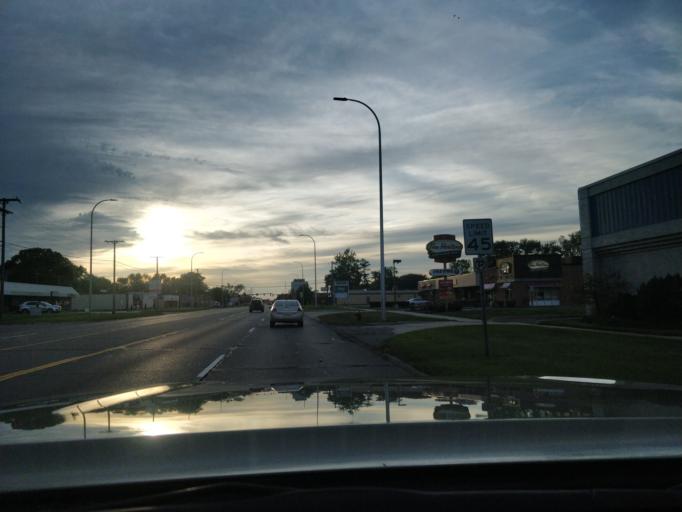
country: US
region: Michigan
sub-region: Wayne County
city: Southgate
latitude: 42.1988
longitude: -83.2245
